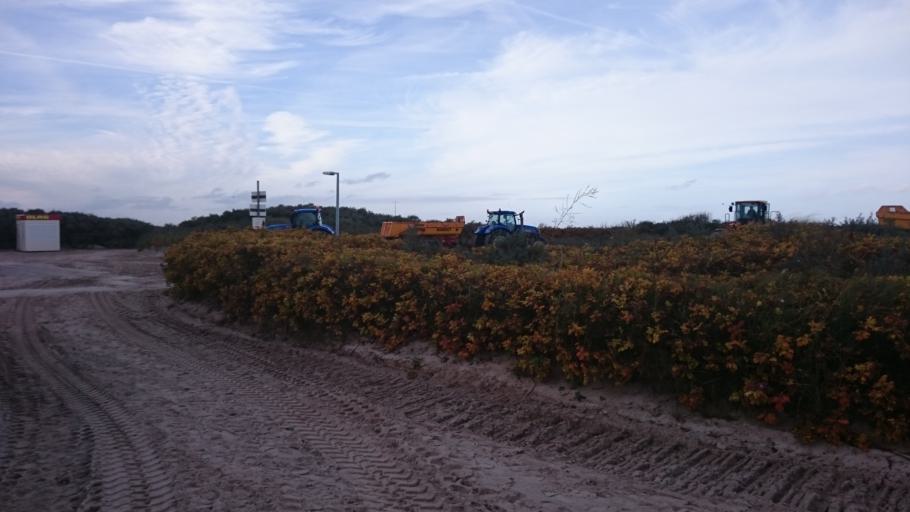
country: DE
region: Schleswig-Holstein
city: Helgoland
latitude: 54.1836
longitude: 7.9111
